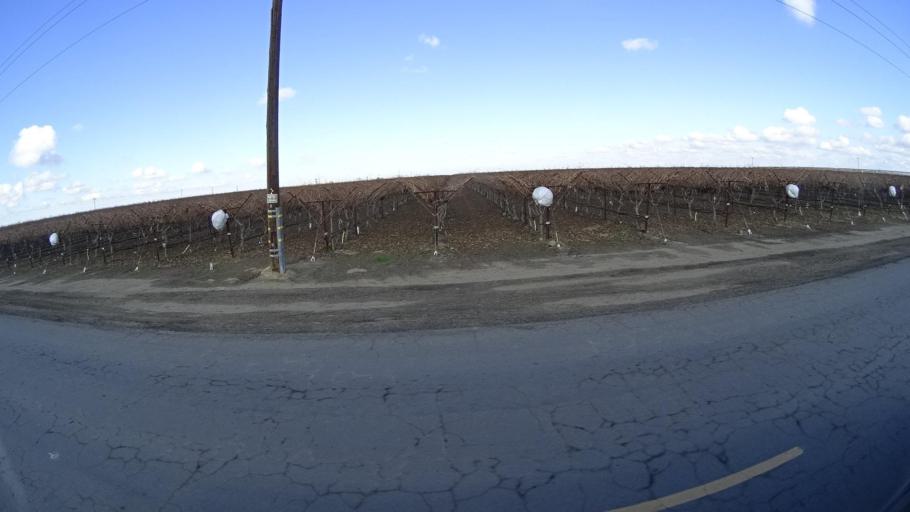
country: US
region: California
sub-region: Kern County
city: McFarland
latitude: 35.6887
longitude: -119.2742
